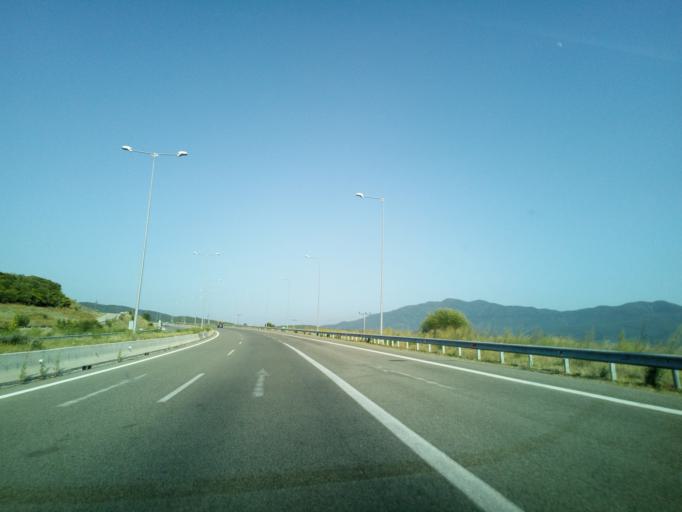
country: GR
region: Central Macedonia
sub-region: Nomos Thessalonikis
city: Stavros
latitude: 40.6756
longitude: 23.5953
